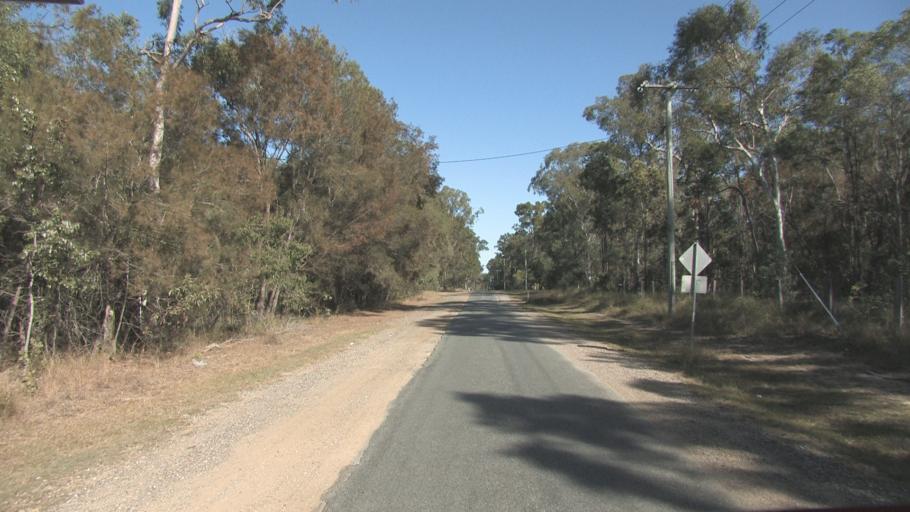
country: AU
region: Queensland
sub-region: Logan
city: Chambers Flat
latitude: -27.7837
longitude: 153.0741
